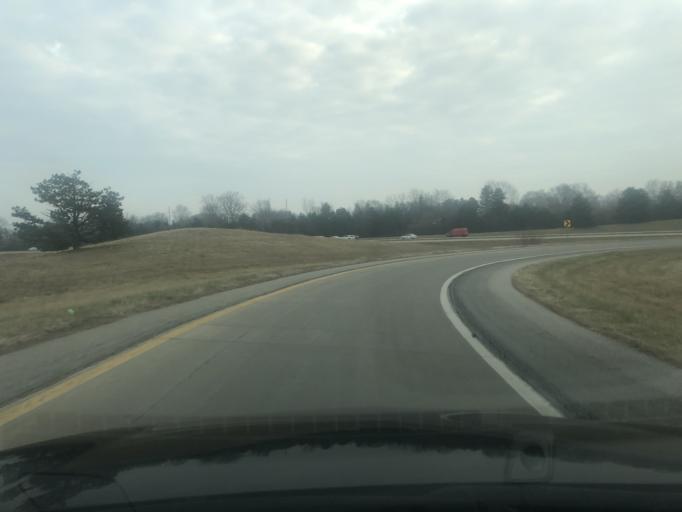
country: US
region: Michigan
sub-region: Wayne County
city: Belleville
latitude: 42.2211
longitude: -83.4834
